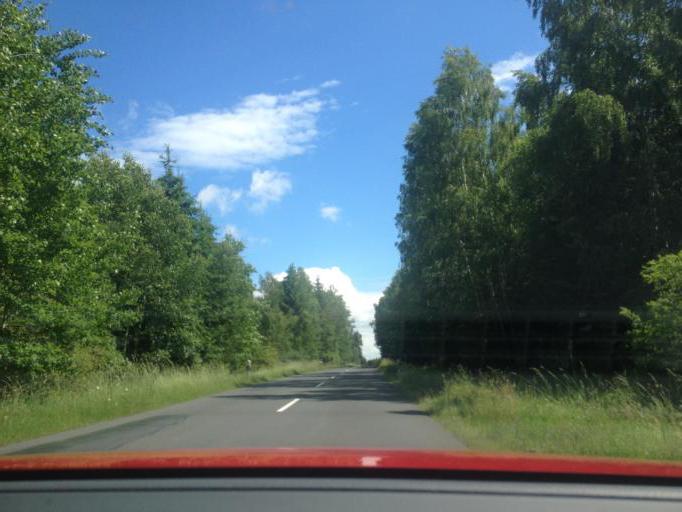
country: DE
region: Bavaria
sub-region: Upper Palatinate
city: Pechbrunn
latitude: 49.9862
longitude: 12.1776
